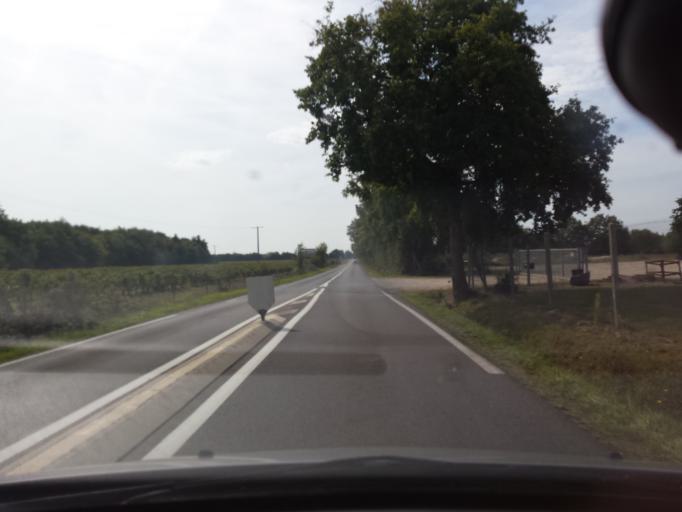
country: FR
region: Pays de la Loire
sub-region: Departement de la Vendee
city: Grosbreuil
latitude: 46.5240
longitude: -1.5529
